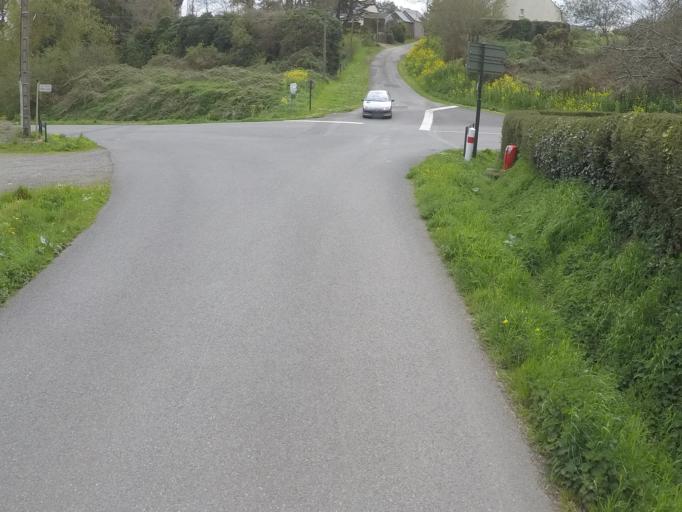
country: FR
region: Brittany
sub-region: Departement des Cotes-d'Armor
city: Plouezec
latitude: 48.7353
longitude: -2.9557
